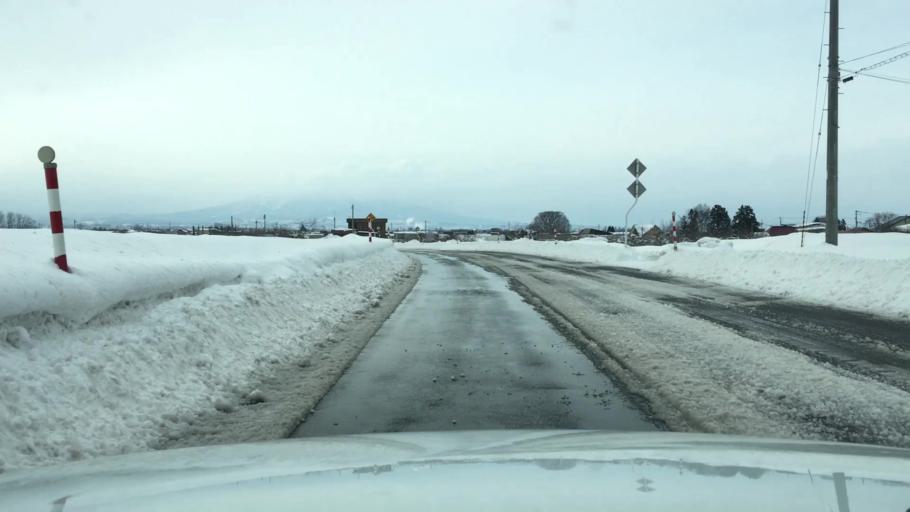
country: JP
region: Aomori
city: Kuroishi
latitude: 40.5929
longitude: 140.5988
